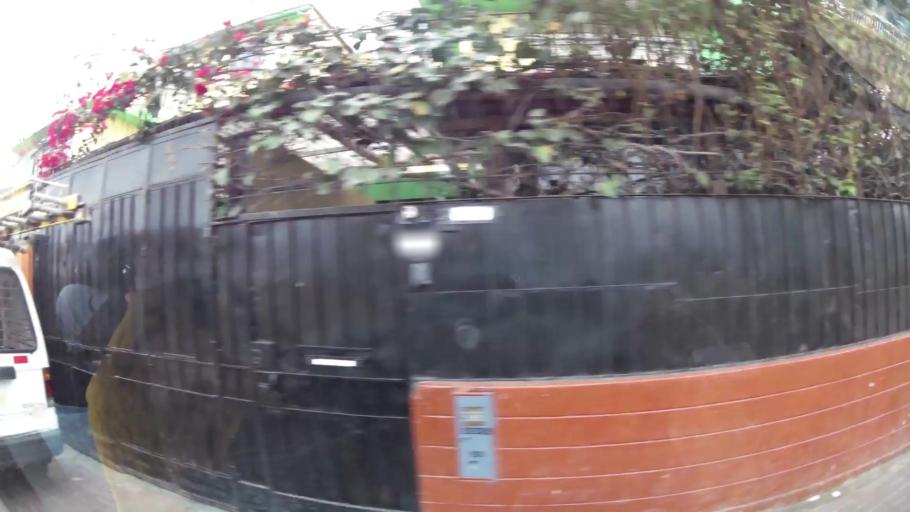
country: PE
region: Lima
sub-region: Lima
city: Surco
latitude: -12.1423
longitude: -77.0181
